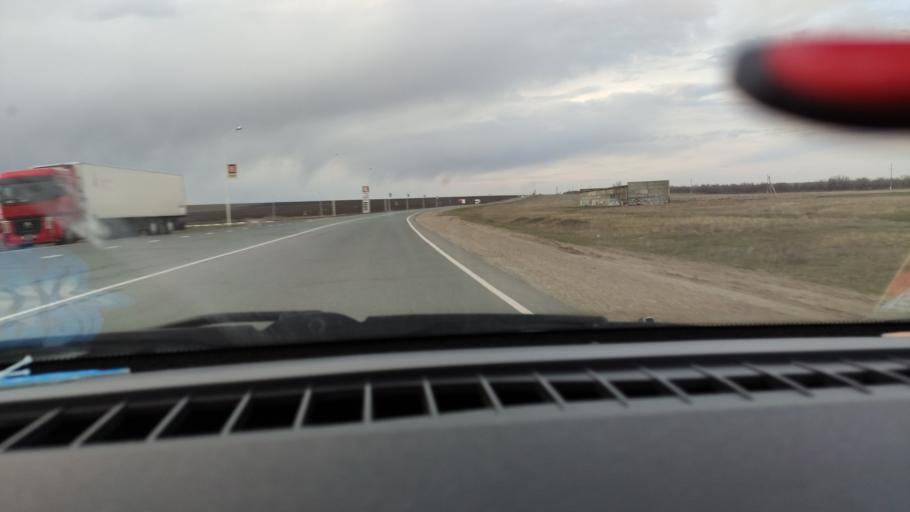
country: RU
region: Saratov
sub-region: Saratovskiy Rayon
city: Saratov
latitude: 51.7381
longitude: 46.0403
